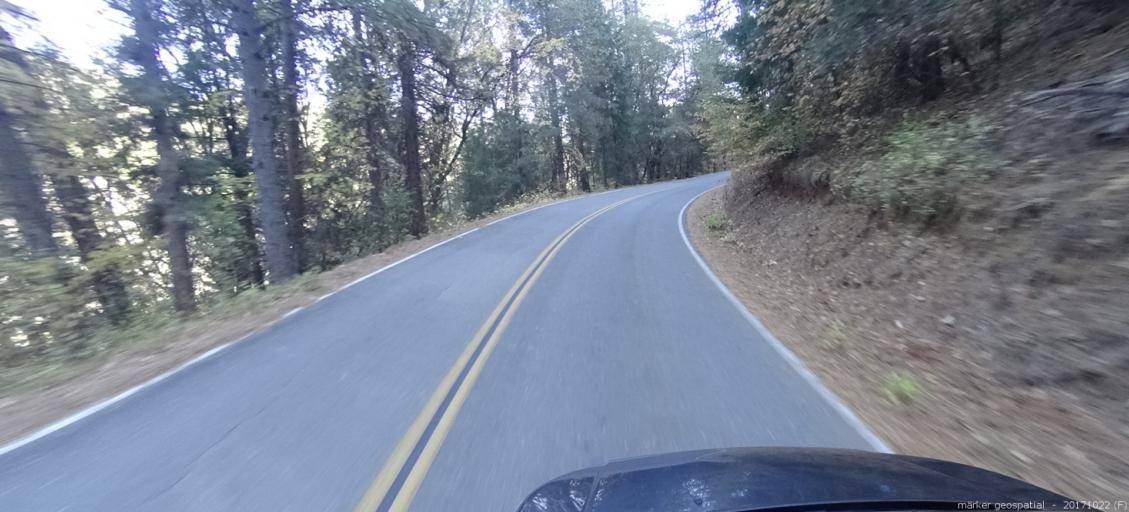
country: US
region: California
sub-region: Shasta County
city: Shasta Lake
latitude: 40.9152
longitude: -122.2437
